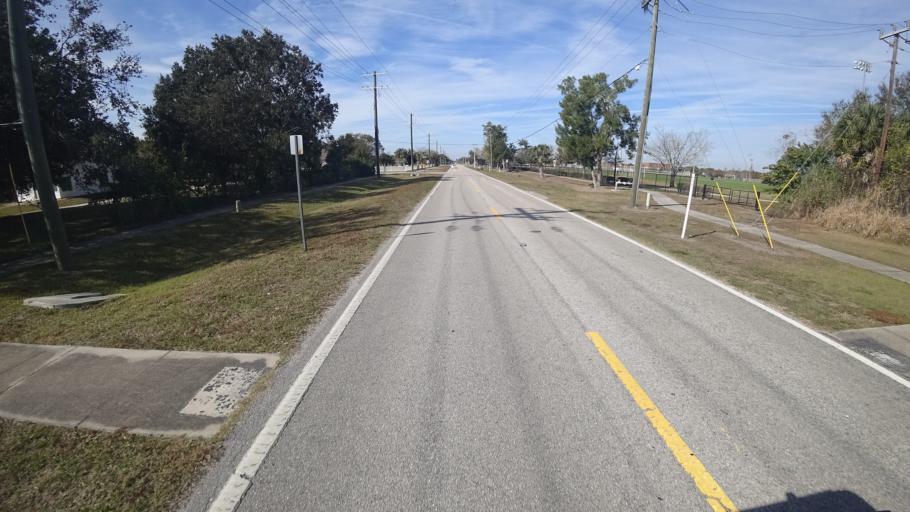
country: US
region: Florida
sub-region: Manatee County
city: Ellenton
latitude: 27.5740
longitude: -82.4841
